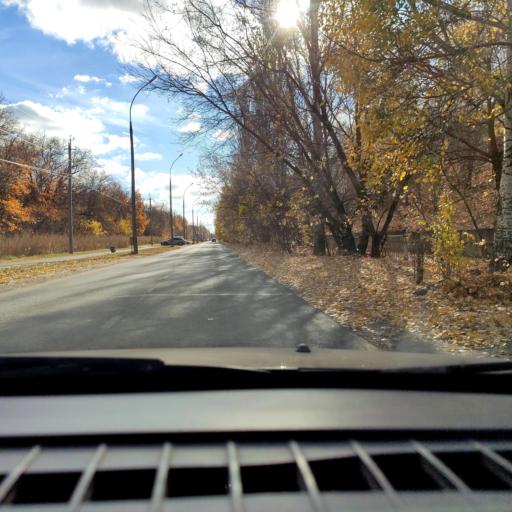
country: RU
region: Samara
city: Tol'yatti
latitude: 53.5119
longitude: 49.3093
